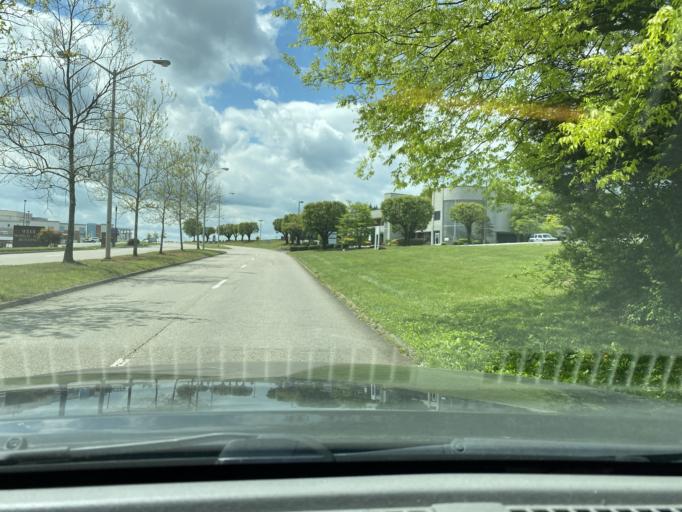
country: US
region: Tennessee
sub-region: Knox County
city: Farragut
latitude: 35.9183
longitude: -84.0969
